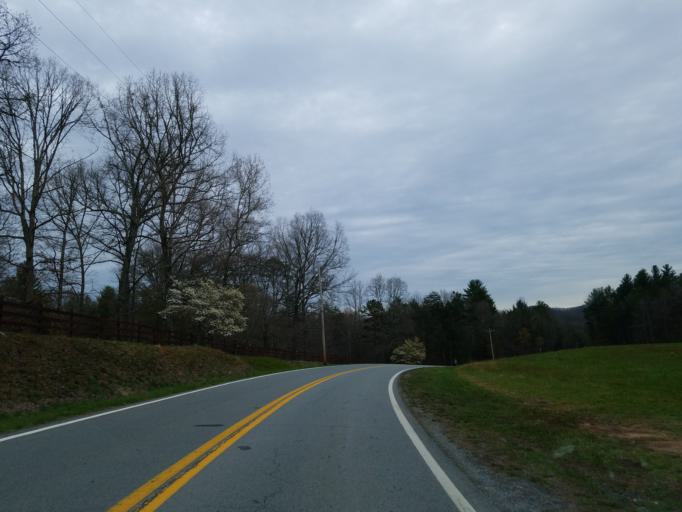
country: US
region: Georgia
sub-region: Fannin County
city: Blue Ridge
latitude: 34.7848
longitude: -84.2470
